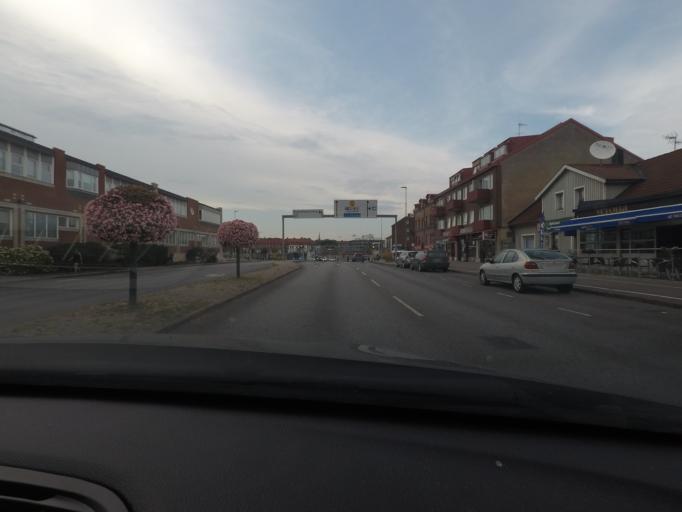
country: SE
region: Halland
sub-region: Halmstads Kommun
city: Halmstad
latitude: 56.6703
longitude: 12.8686
